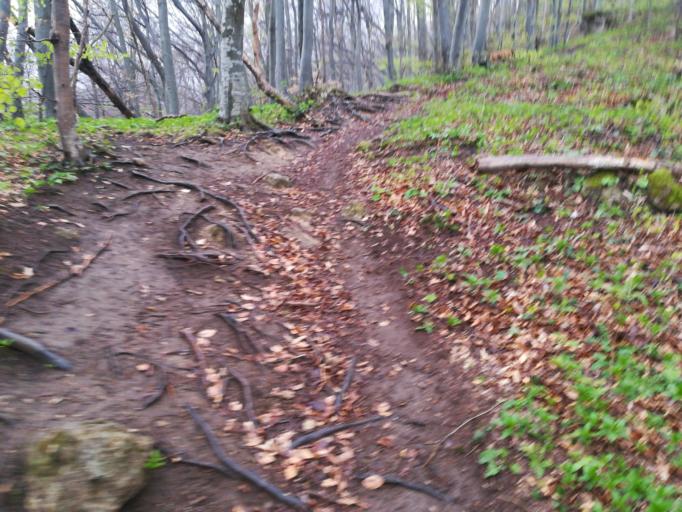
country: HR
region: Varazdinska
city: Ivanec
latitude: 46.1922
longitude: 16.1395
